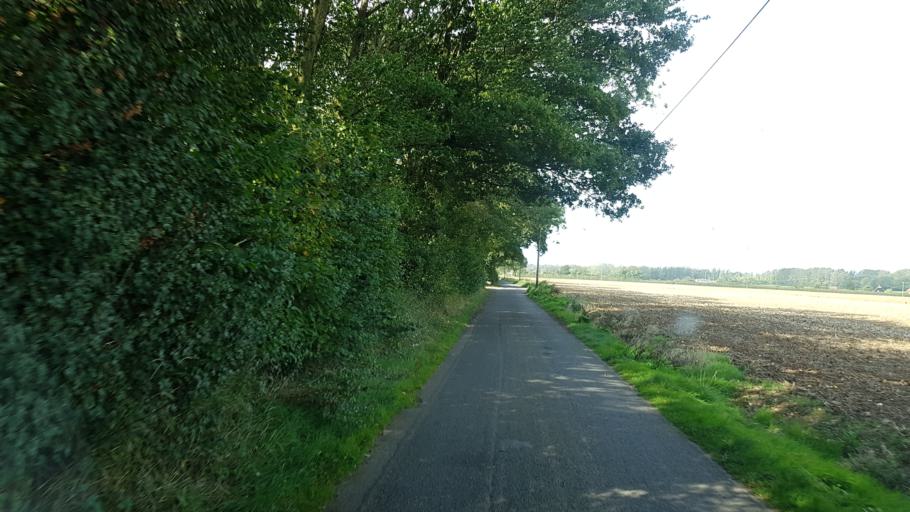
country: GB
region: England
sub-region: Kent
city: Harrietsham
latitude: 51.2379
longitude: 0.6105
